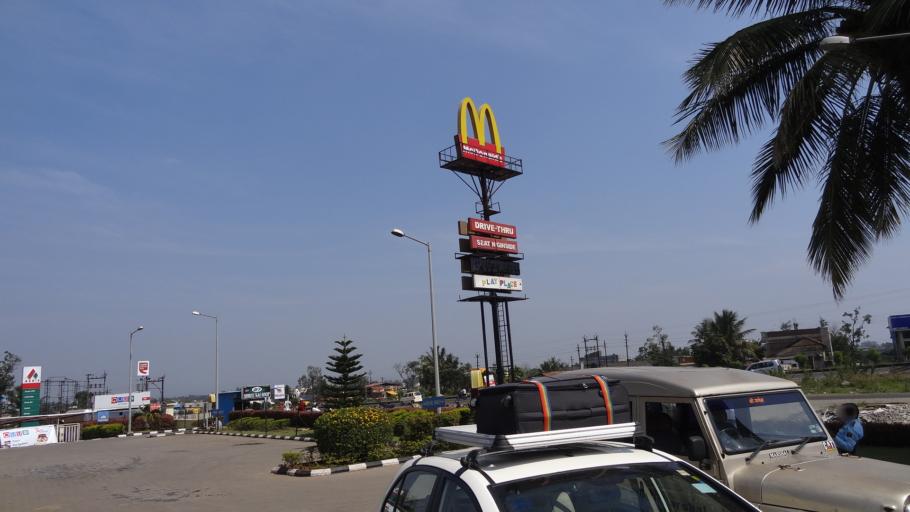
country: IN
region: Maharashtra
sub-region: Kolhapur
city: Kolhapur
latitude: 16.6867
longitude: 74.2727
